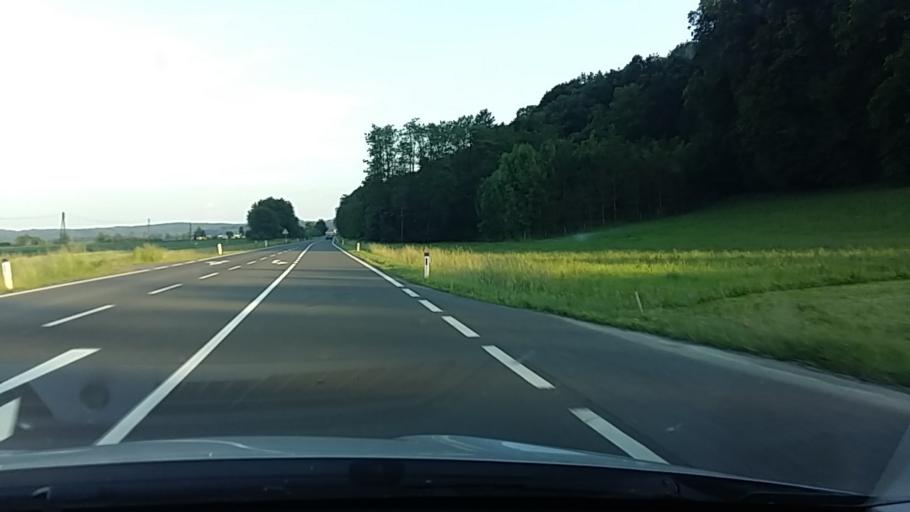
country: AT
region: Styria
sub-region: Politischer Bezirk Suedoststeiermark
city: Hatzendorf
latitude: 46.9657
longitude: 16.0129
